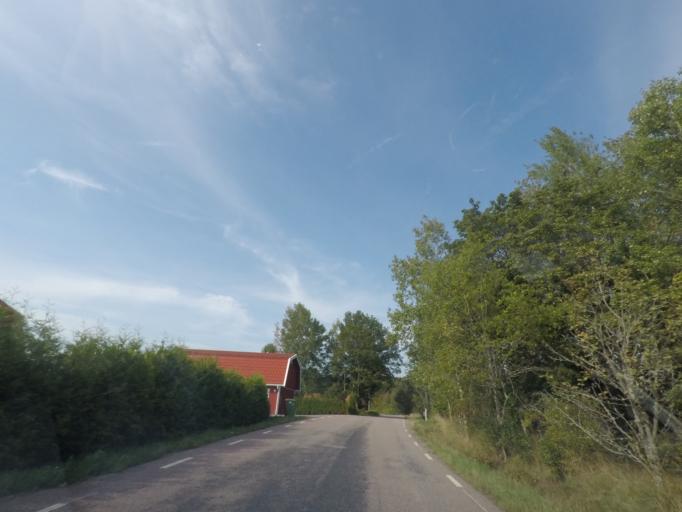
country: SE
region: Vaestmanland
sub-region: Hallstahammars Kommun
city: Kolback
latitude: 59.5322
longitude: 16.1534
